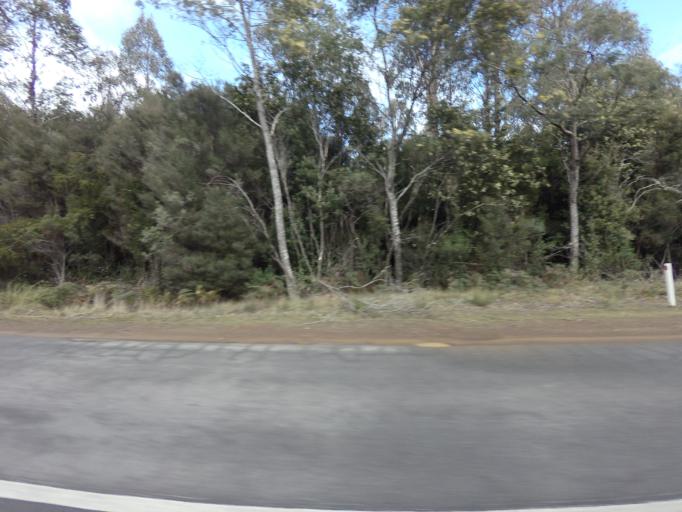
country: AU
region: Tasmania
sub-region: Huon Valley
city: Geeveston
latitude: -43.3976
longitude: 146.9563
